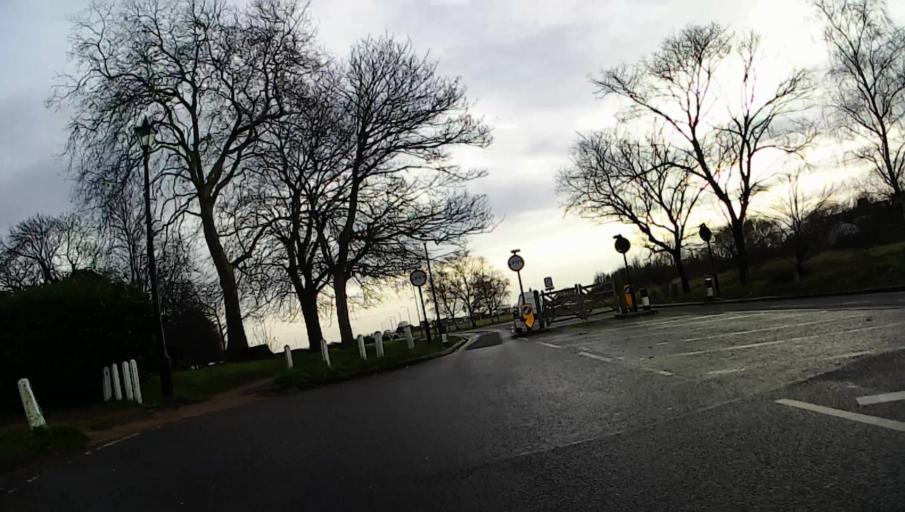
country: GB
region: England
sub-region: Greater London
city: Blackheath
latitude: 51.4750
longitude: -0.0039
